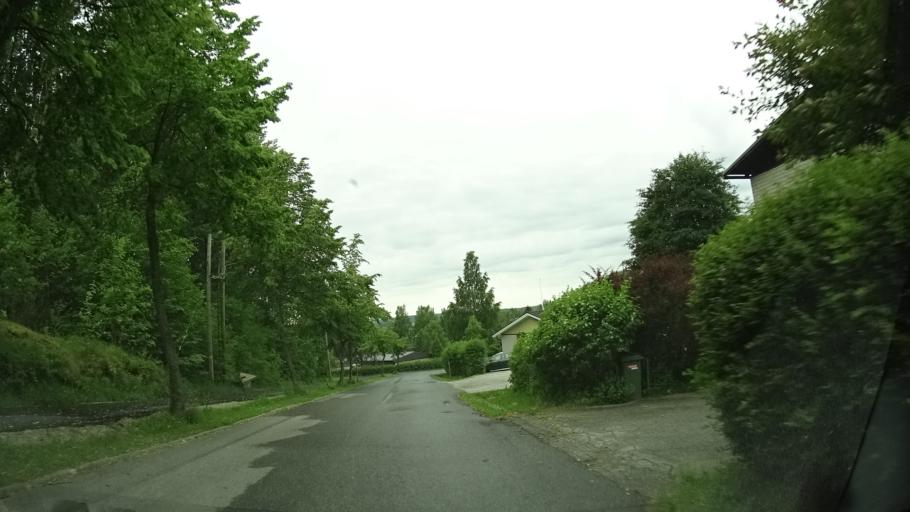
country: FI
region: Varsinais-Suomi
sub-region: Salo
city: Halikko
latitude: 60.4046
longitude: 23.0770
